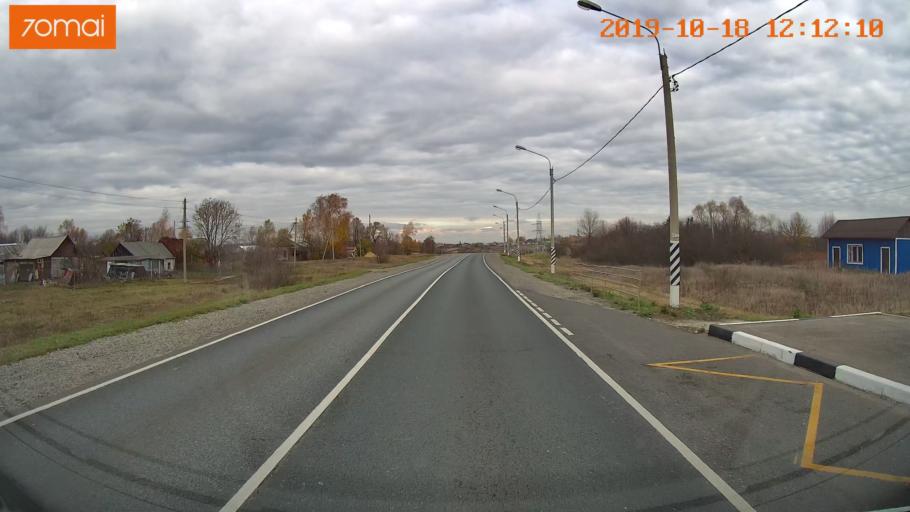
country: RU
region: Rjazan
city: Zakharovo
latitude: 54.4089
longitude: 39.3559
